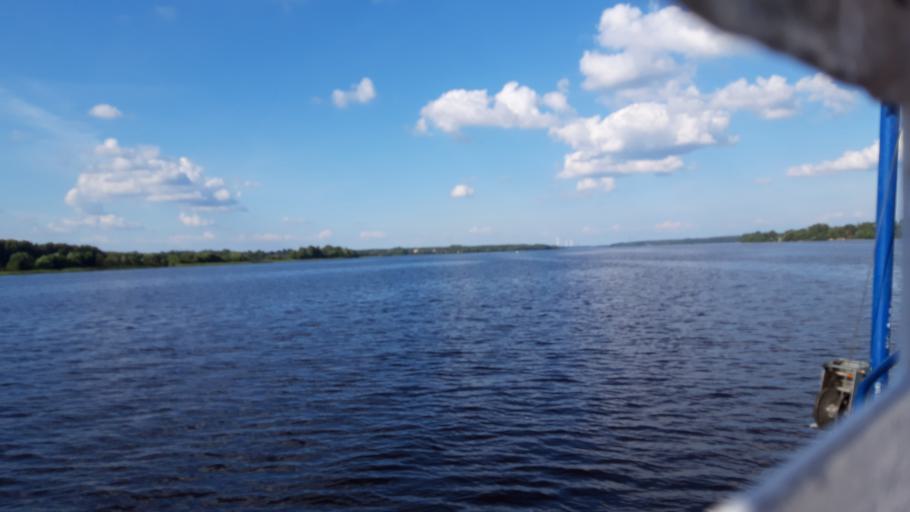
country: RU
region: Tverskaya
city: Konakovo
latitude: 56.6554
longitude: 36.6364
